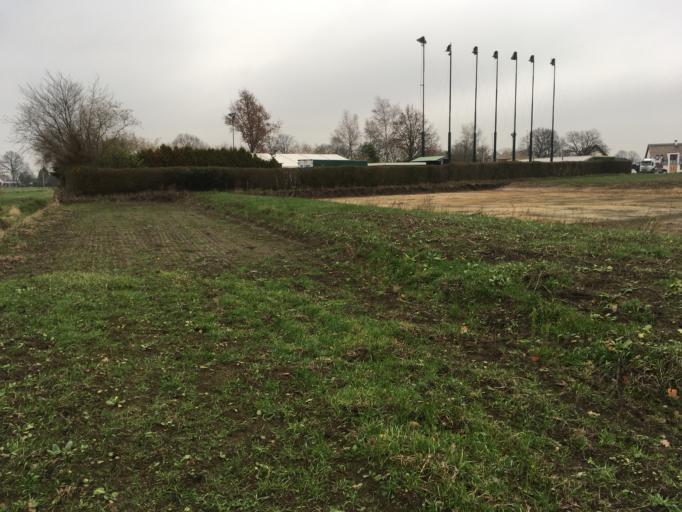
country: NL
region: North Brabant
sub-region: Gemeente Tilburg
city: Tilburg
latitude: 51.5912
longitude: 5.1274
